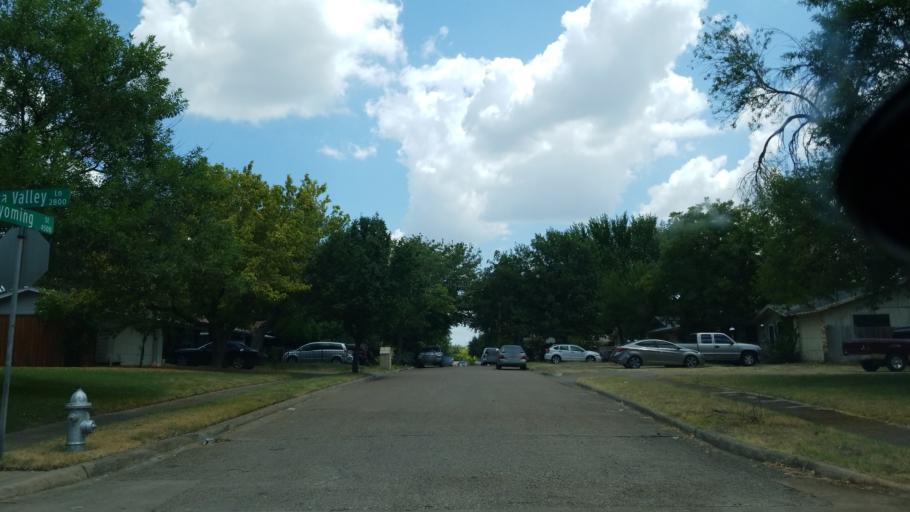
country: US
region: Texas
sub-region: Dallas County
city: Cockrell Hill
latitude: 32.7144
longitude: -96.8960
